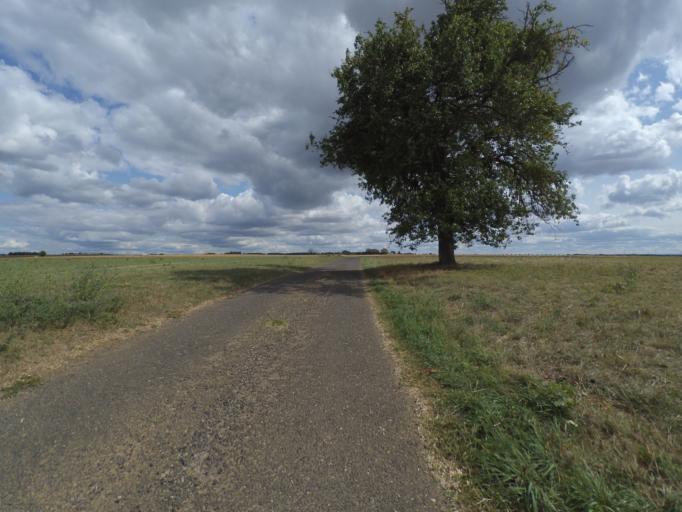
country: LU
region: Luxembourg
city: Aspelt
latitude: 49.5401
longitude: 6.2309
